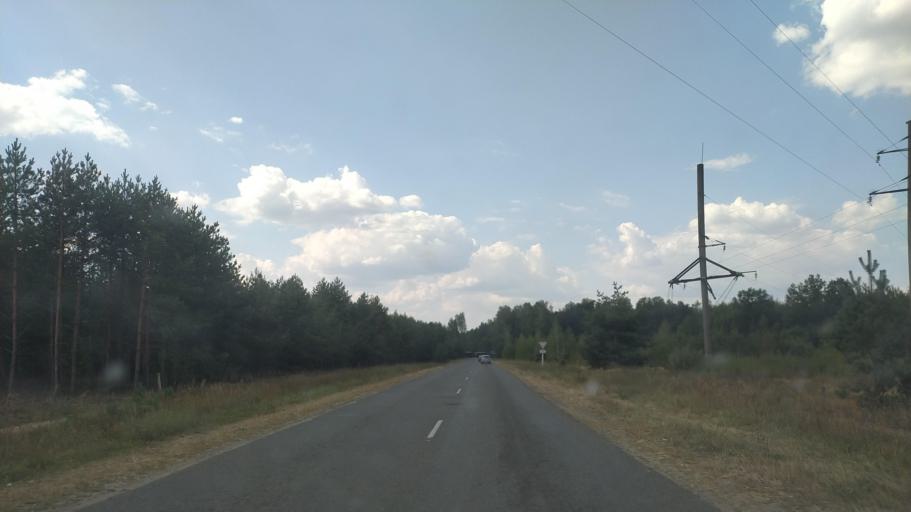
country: BY
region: Brest
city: Drahichyn
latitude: 52.1057
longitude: 25.1193
